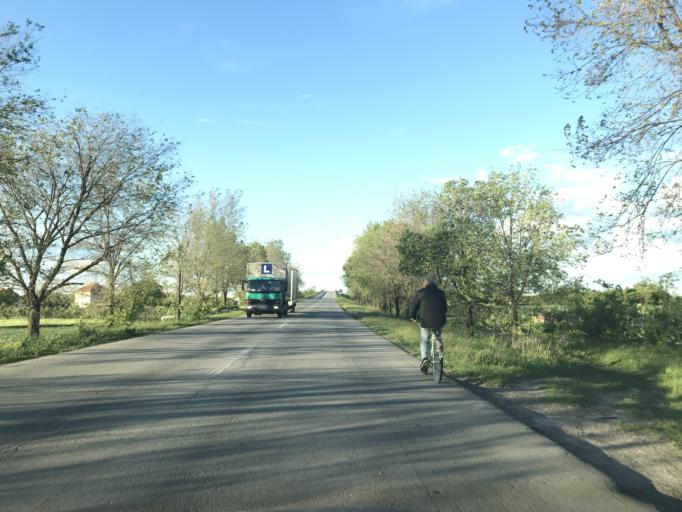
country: RS
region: Autonomna Pokrajina Vojvodina
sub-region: Srednjebanatski Okrug
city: Zrenjanin
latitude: 45.3940
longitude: 20.3558
